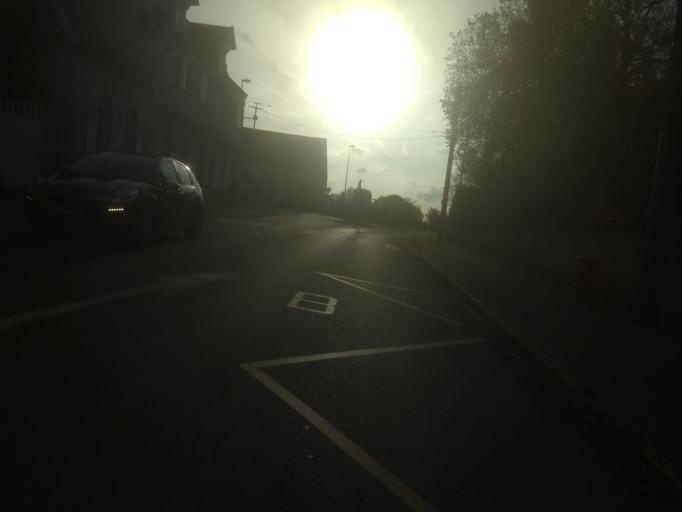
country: FR
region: Nord-Pas-de-Calais
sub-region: Departement du Pas-de-Calais
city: Agny
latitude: 50.2649
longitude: 2.7521
